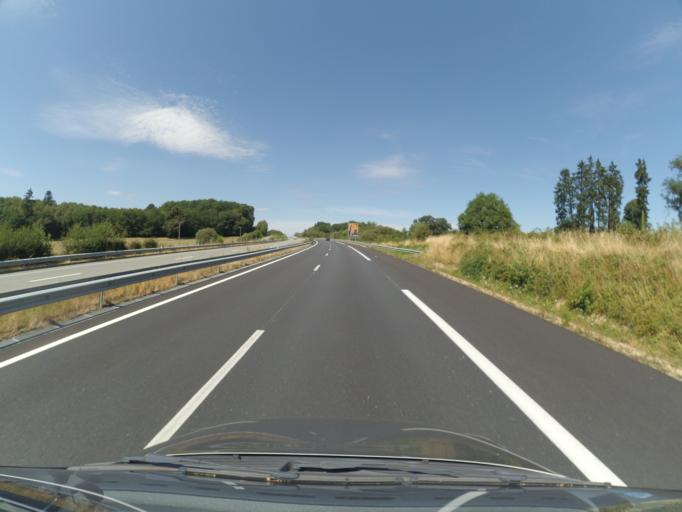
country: FR
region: Limousin
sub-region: Departement de la Creuse
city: Saint-Agnant-de-Versillat
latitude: 46.2324
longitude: 1.5479
